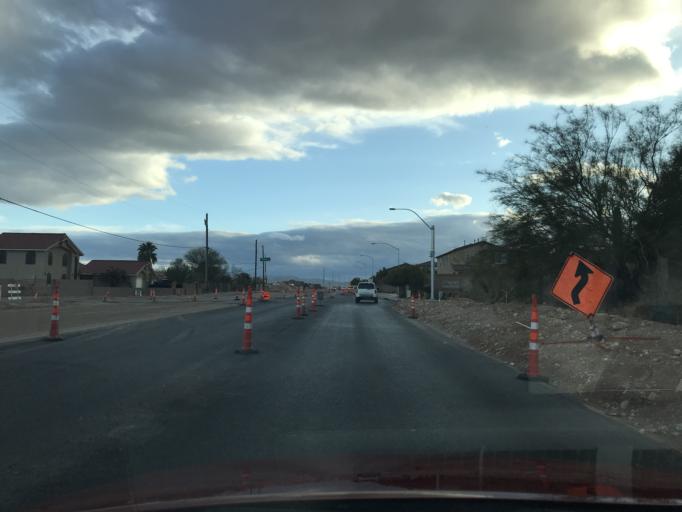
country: US
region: Nevada
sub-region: Clark County
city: Enterprise
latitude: 36.0340
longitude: -115.2790
